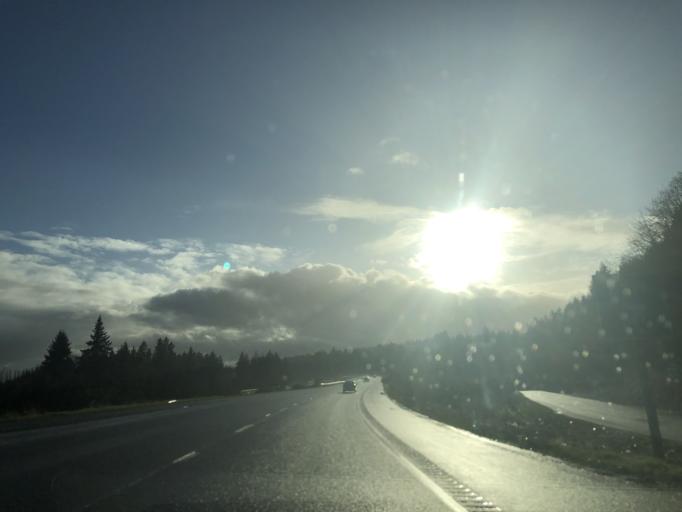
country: US
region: Washington
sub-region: Kitsap County
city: Silverdale
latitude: 47.6389
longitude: -122.7057
